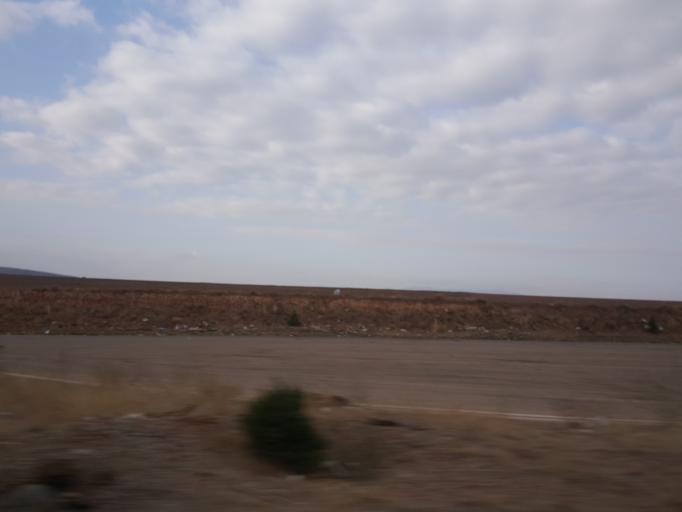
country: TR
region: Kirikkale
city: Keskin
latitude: 39.6182
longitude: 33.6534
